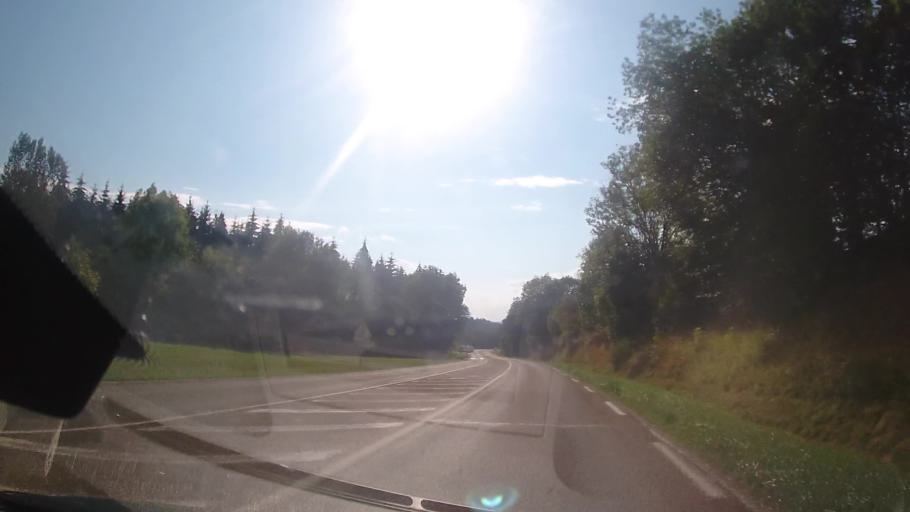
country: FR
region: Franche-Comte
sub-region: Departement du Jura
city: Clairvaux-les-Lacs
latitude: 46.5830
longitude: 5.8001
